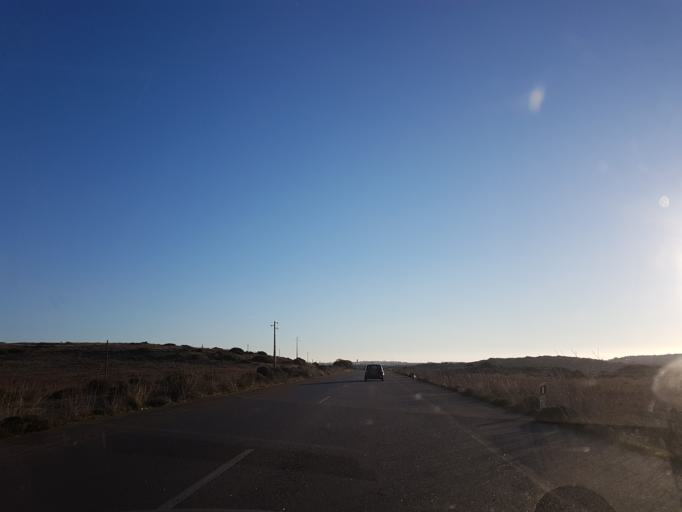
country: PT
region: Faro
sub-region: Vila do Bispo
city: Sagres
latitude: 37.0327
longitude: -8.9353
